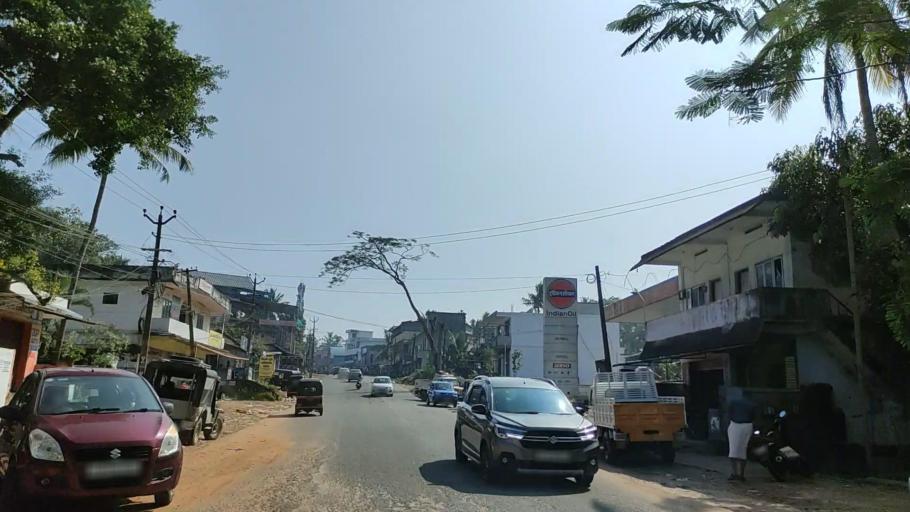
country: IN
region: Kerala
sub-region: Kollam
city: Punalur
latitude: 8.9296
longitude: 76.9293
